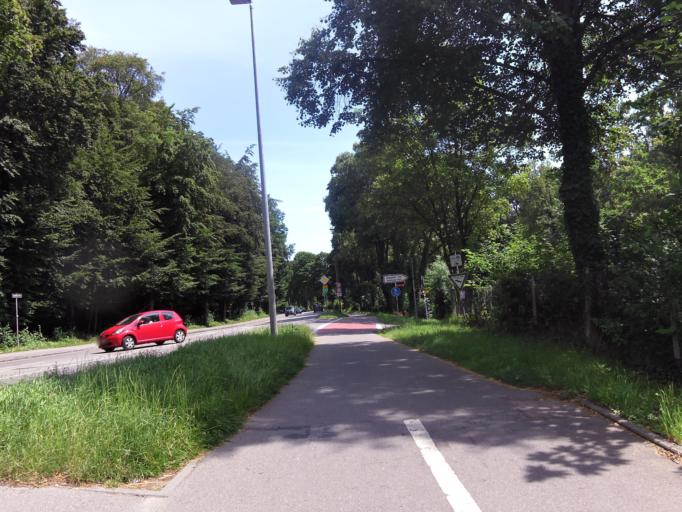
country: DE
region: Baden-Wuerttemberg
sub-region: Tuebingen Region
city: Friedrichshafen
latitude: 47.6613
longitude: 9.4341
